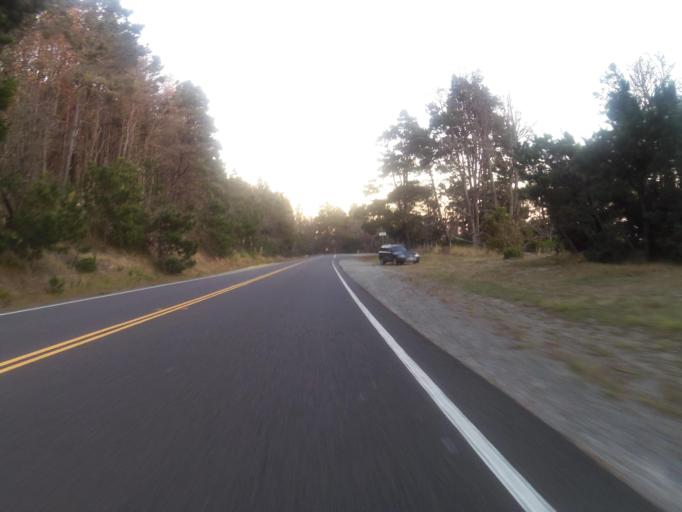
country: US
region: California
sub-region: Sonoma County
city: Sea Ranch
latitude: 38.6050
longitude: -123.3589
